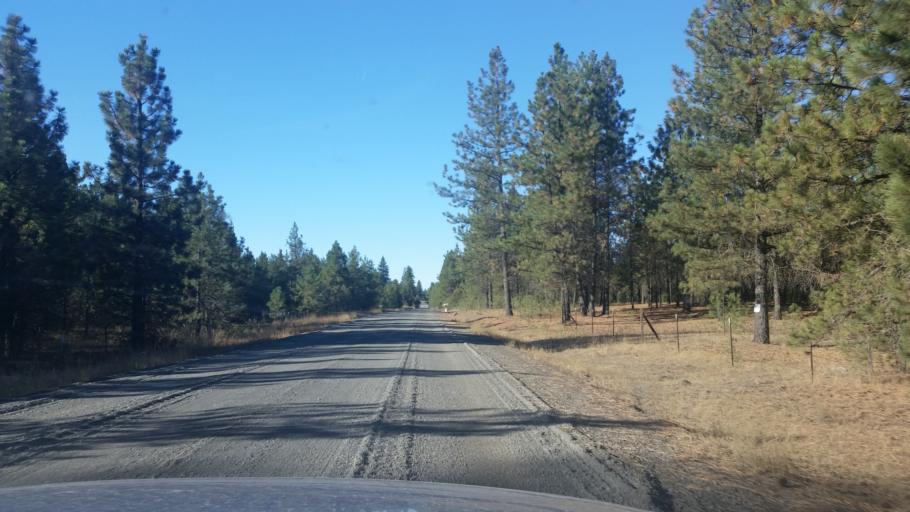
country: US
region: Washington
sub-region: Spokane County
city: Medical Lake
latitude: 47.4303
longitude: -117.7853
